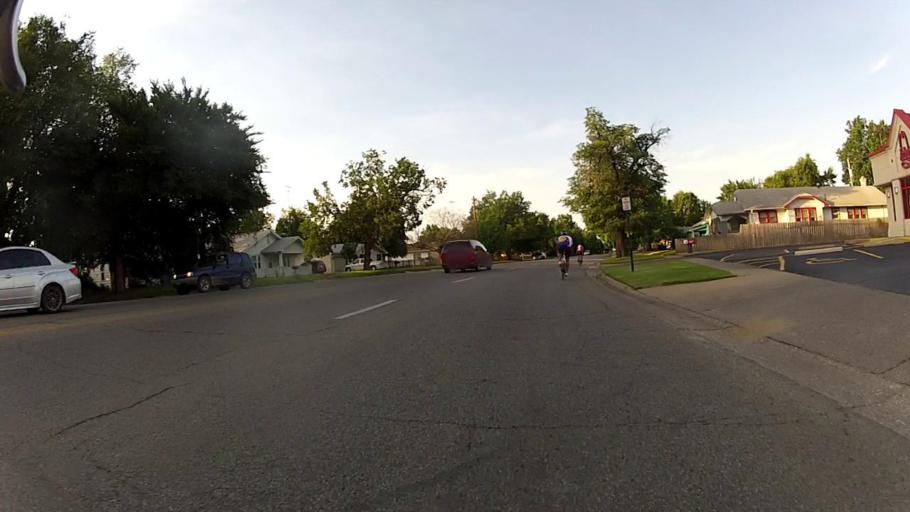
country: US
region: Kansas
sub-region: Cowley County
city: Arkansas City
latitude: 37.0774
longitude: -97.0393
